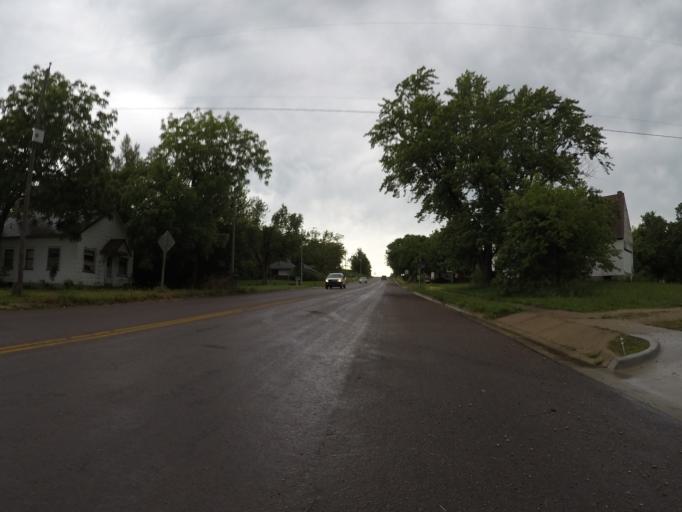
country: US
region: Kansas
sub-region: Wabaunsee County
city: Alma
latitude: 38.8596
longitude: -96.1105
